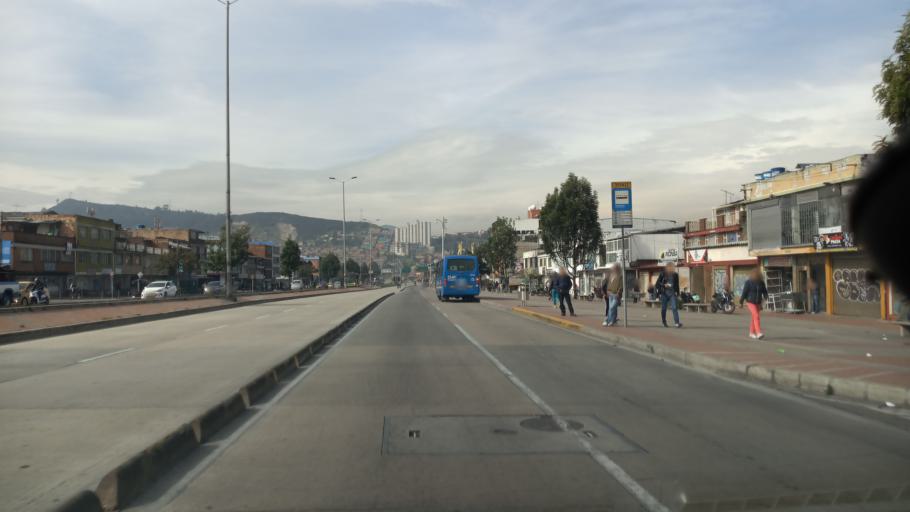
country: CO
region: Bogota D.C.
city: Bogota
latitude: 4.5746
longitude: -74.0958
